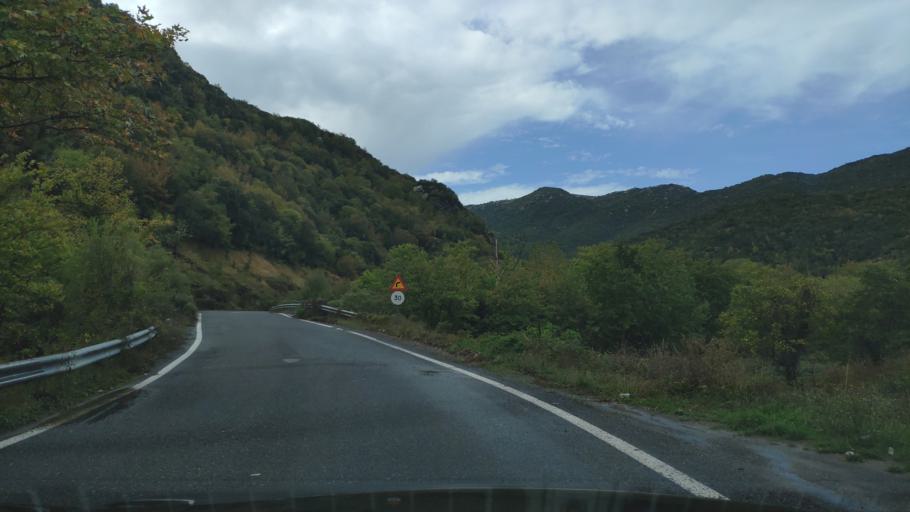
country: GR
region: Peloponnese
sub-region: Nomos Arkadias
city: Dimitsana
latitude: 37.6222
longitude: 22.0505
